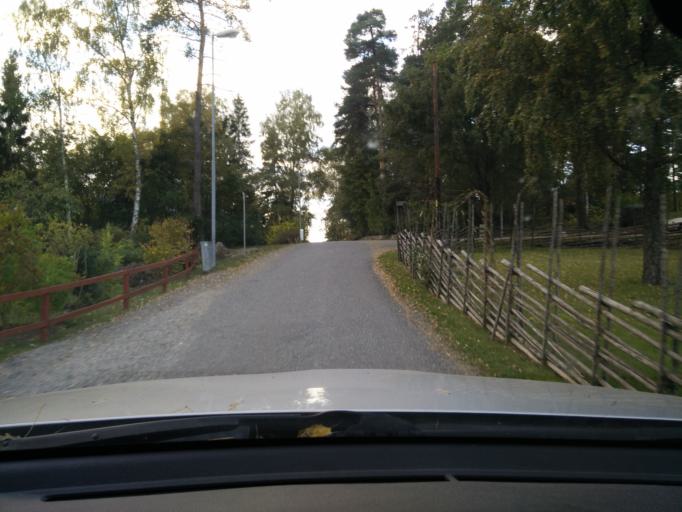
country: SE
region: Stockholm
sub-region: Stockholms Kommun
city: Kista
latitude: 59.4109
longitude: 17.9555
